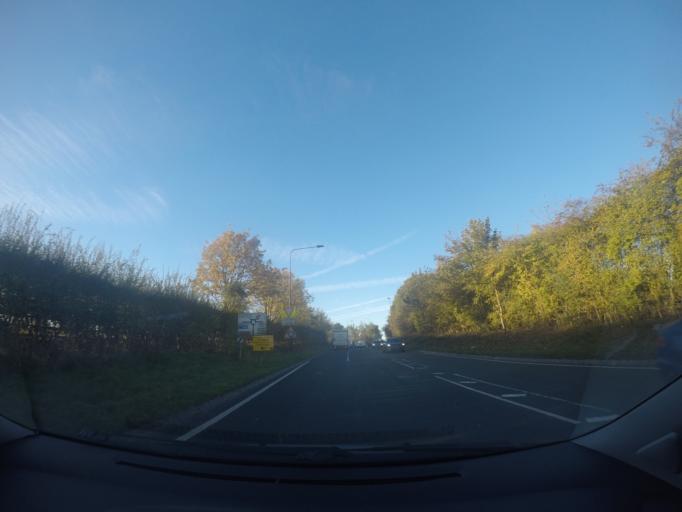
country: GB
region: England
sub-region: City of York
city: Copmanthorpe
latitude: 53.9217
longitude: -1.1506
